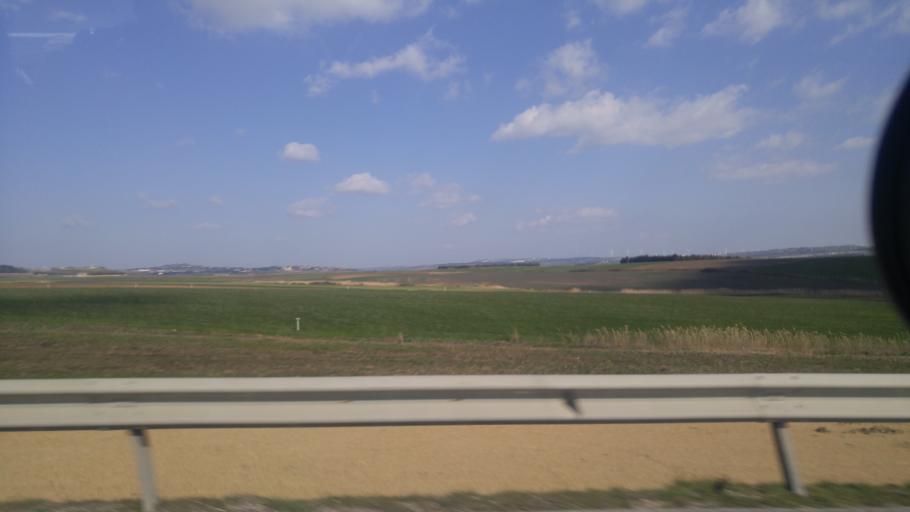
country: TR
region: Istanbul
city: Canta
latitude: 41.1299
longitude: 28.1595
